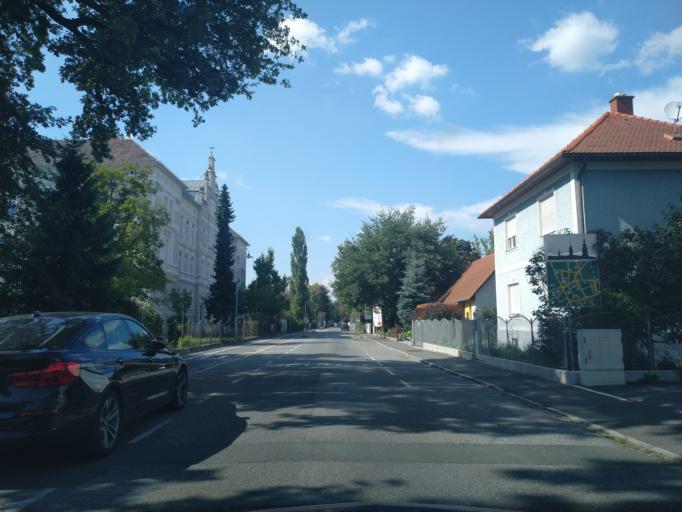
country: AT
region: Styria
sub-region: Politischer Bezirk Leibnitz
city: Leibnitz
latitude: 46.7793
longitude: 15.5430
